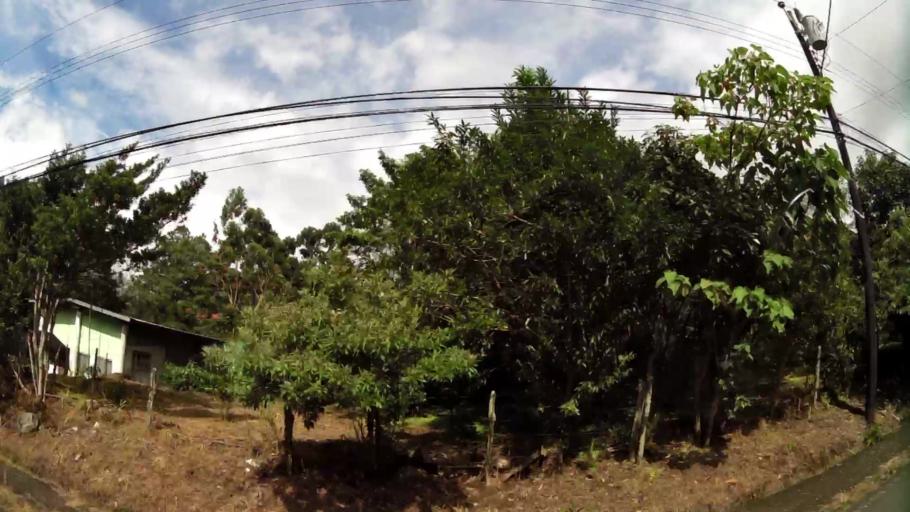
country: PA
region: Chiriqui
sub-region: Distrito Boquete
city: Boquete
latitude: 8.8006
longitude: -82.4260
